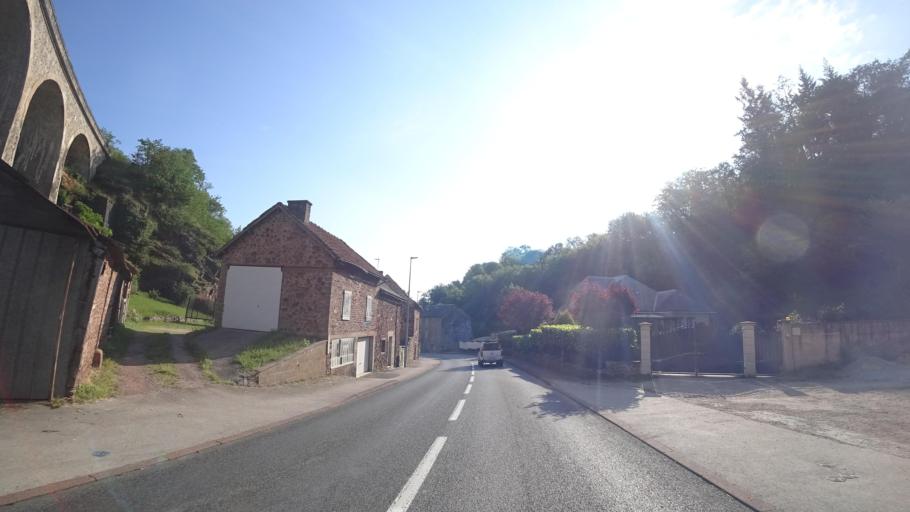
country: FR
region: Midi-Pyrenees
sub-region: Departement de l'Aveyron
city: Olemps
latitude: 44.3357
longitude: 2.5600
